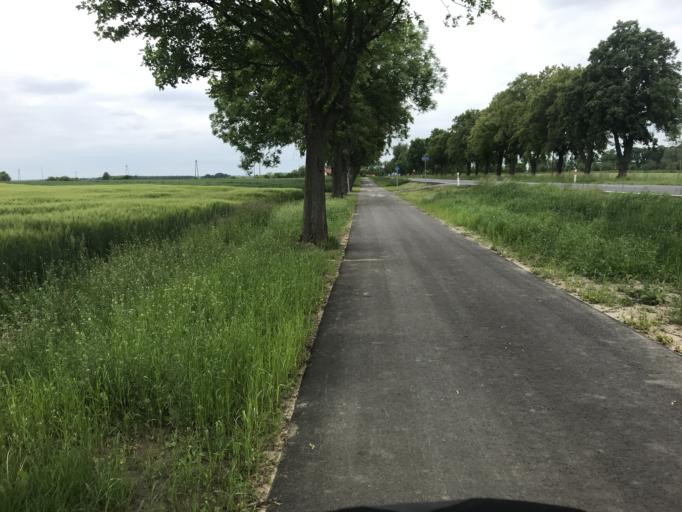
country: PL
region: Lubusz
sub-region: Powiat gorzowski
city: Kostrzyn nad Odra
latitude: 52.6674
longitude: 14.6551
